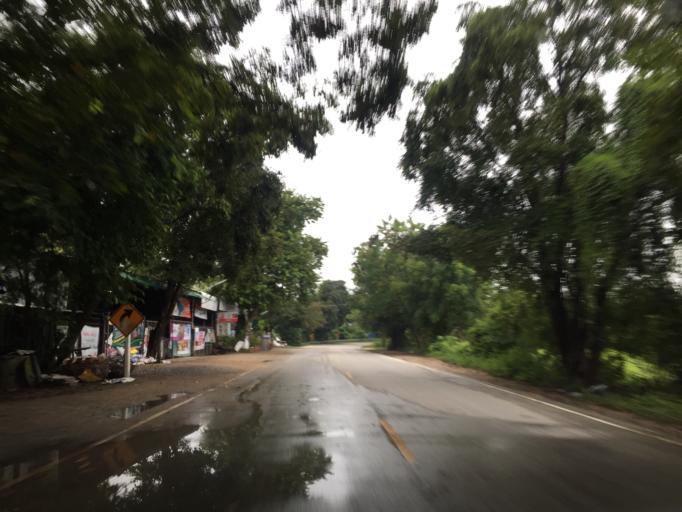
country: TH
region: Lamphun
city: Ban Thi
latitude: 18.6703
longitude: 99.0903
